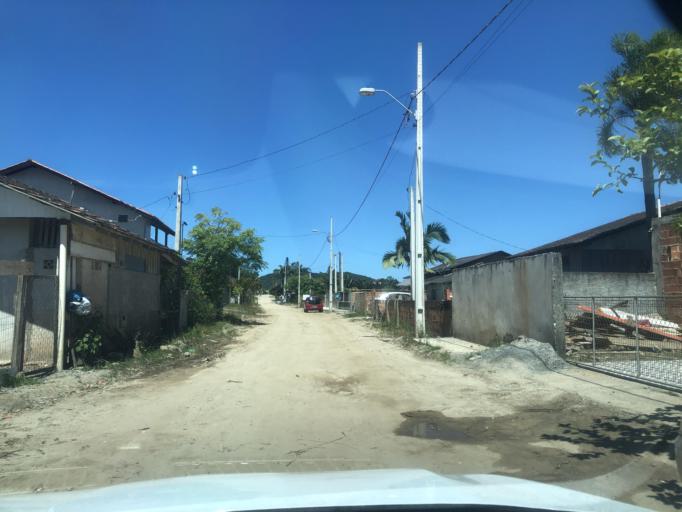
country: BR
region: Santa Catarina
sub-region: Sao Francisco Do Sul
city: Sao Francisco do Sul
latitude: -26.2261
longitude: -48.5232
